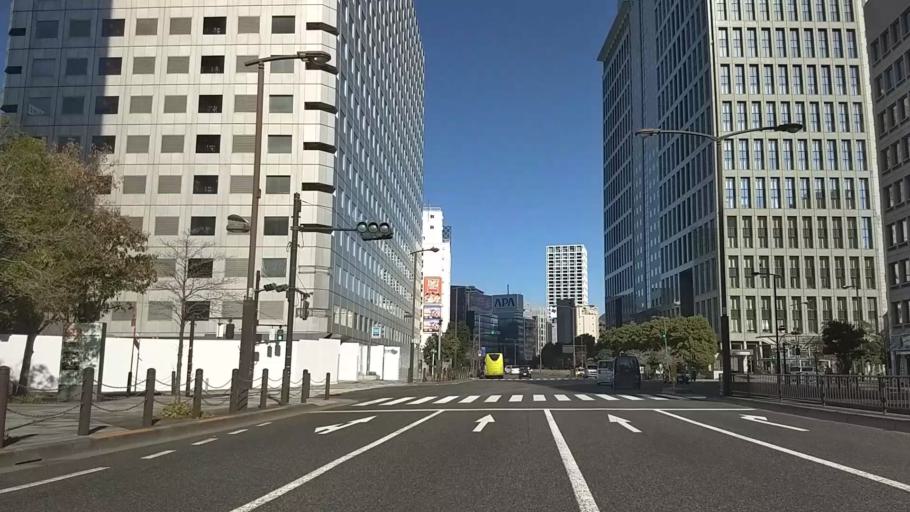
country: JP
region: Tokyo
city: Tokyo
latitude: 35.6714
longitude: 139.7420
